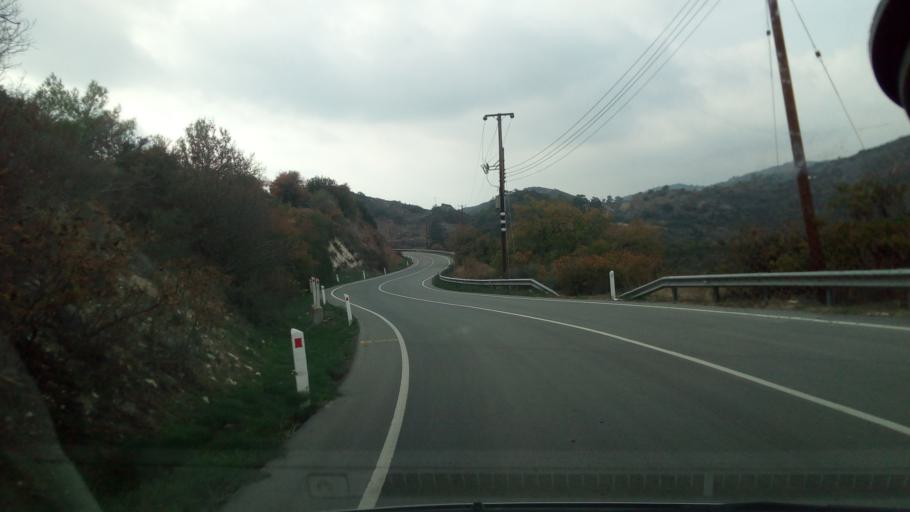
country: CY
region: Lefkosia
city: Lythrodontas
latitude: 34.8703
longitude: 33.2878
